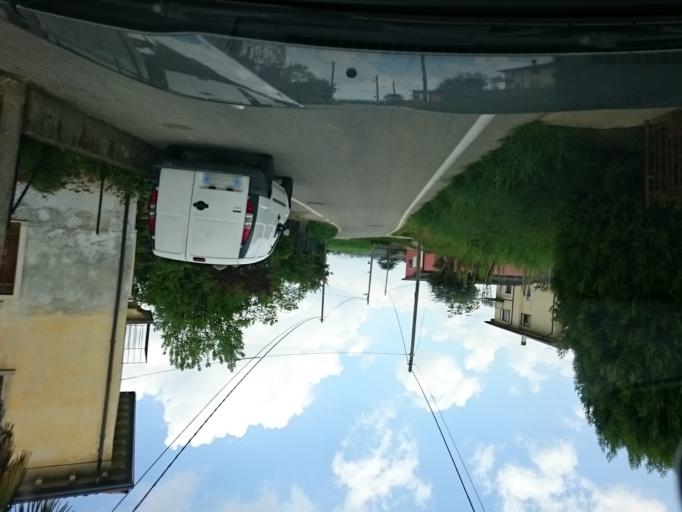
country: IT
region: Veneto
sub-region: Provincia di Vicenza
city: Torri di Quartesolo
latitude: 45.5191
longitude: 11.5860
